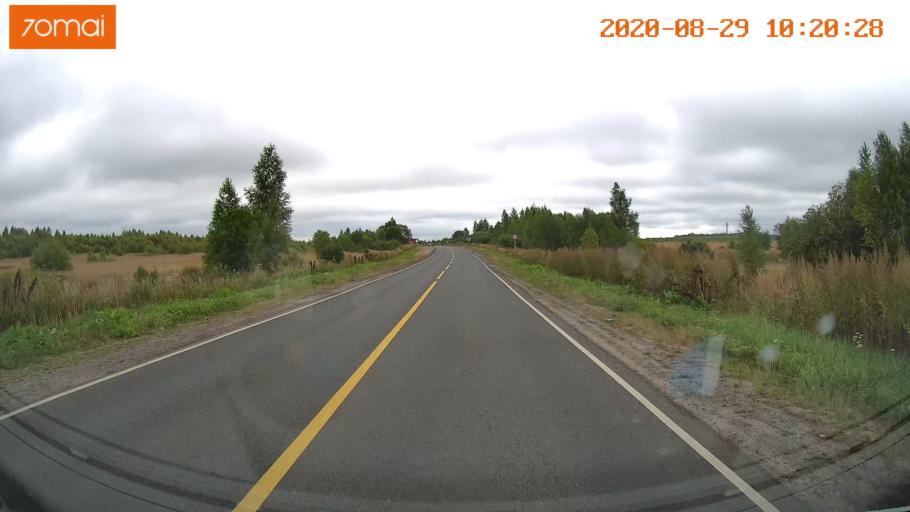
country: RU
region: Ivanovo
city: Yur'yevets
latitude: 57.3236
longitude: 42.8862
